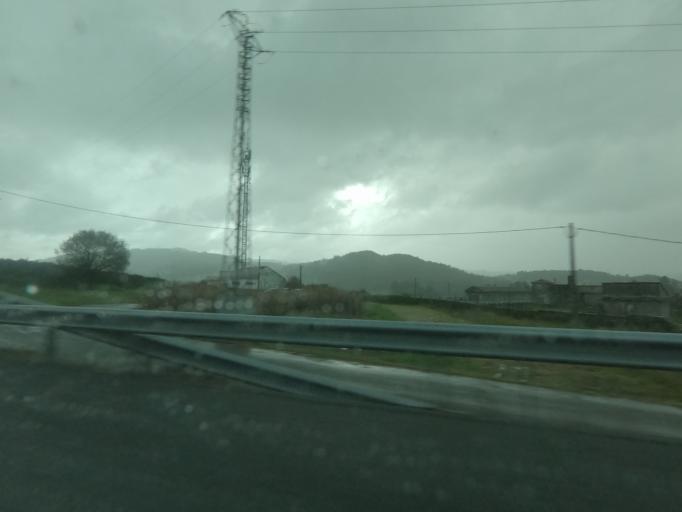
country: ES
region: Galicia
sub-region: Provincia de Pontevedra
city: Marin
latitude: 42.3607
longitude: -8.6401
